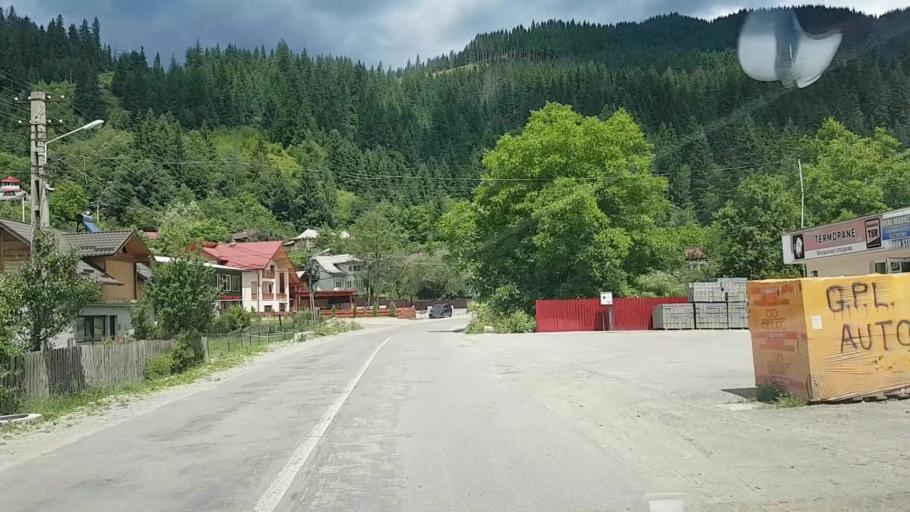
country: RO
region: Suceava
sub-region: Comuna Brosteni
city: Brosteni
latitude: 47.2424
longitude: 25.7020
